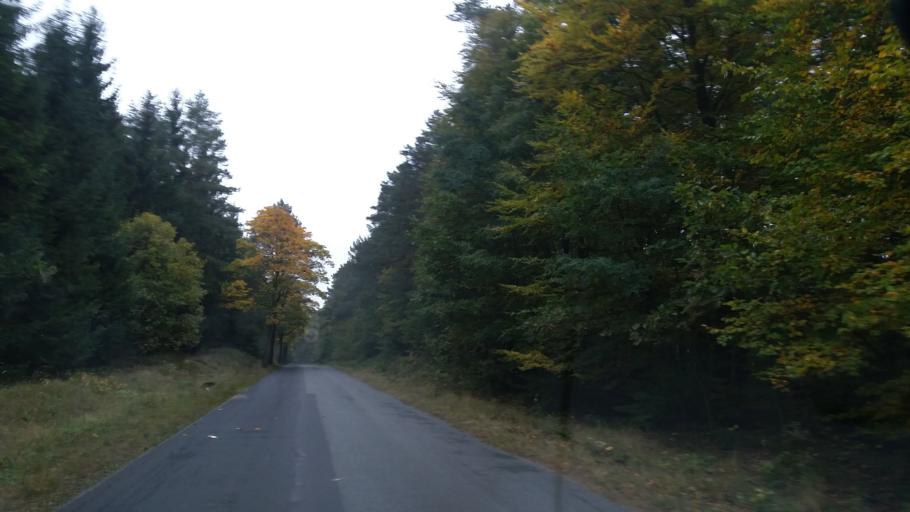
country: PL
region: Lubusz
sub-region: Powiat strzelecko-drezdenecki
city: Dobiegniew
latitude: 53.0621
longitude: 15.7626
